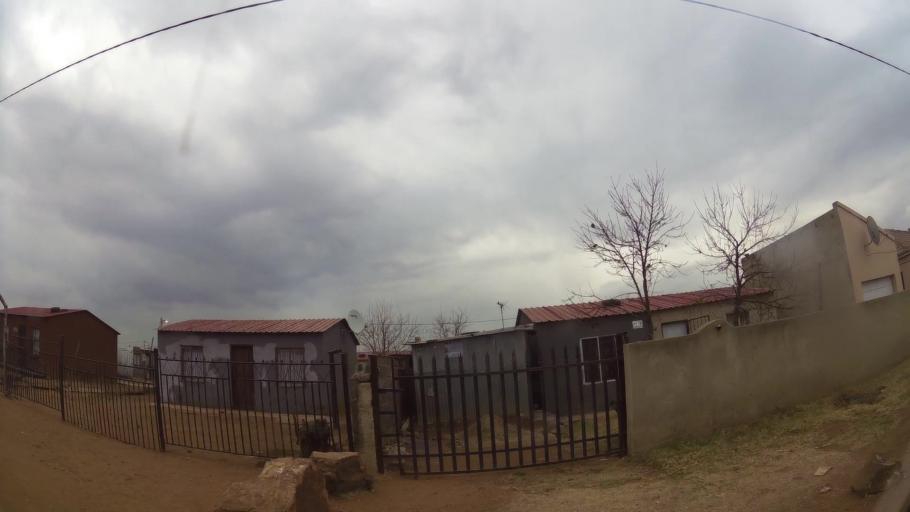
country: ZA
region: Gauteng
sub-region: Ekurhuleni Metropolitan Municipality
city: Germiston
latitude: -26.3836
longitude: 28.1395
